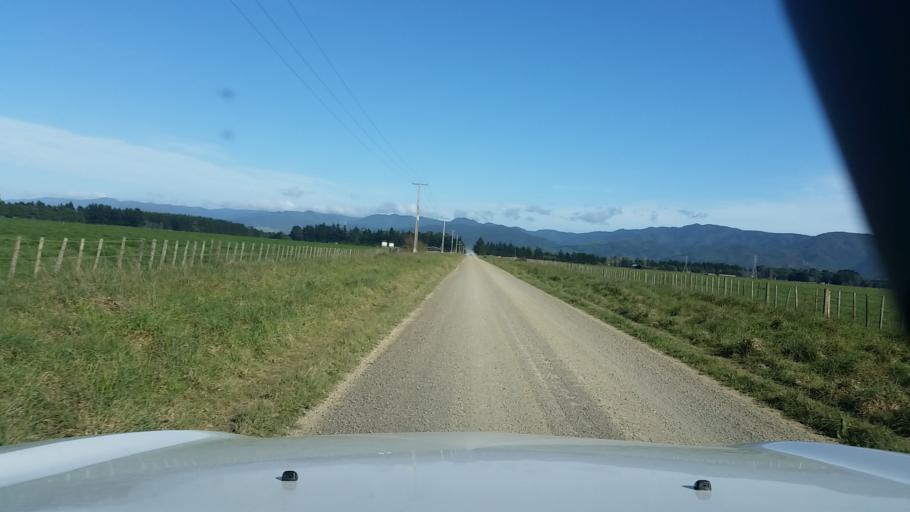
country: NZ
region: Wellington
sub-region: Masterton District
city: Masterton
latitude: -41.1188
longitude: 175.4039
